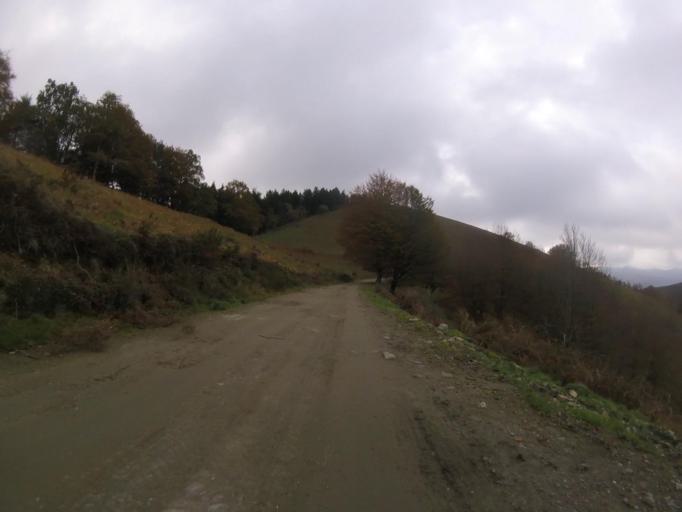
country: ES
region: Navarre
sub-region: Provincia de Navarra
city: Goizueta
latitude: 43.2050
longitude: -1.8245
